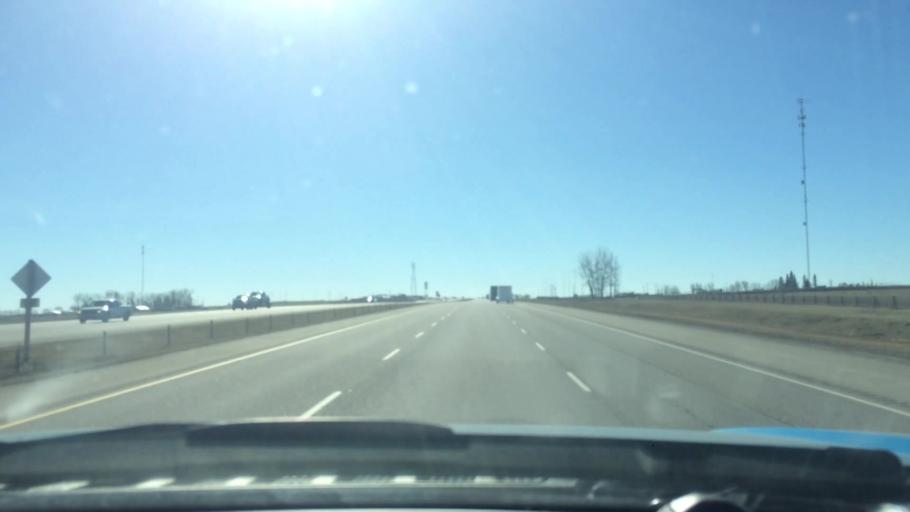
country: CA
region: Alberta
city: Crossfield
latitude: 51.4232
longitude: -114.0021
